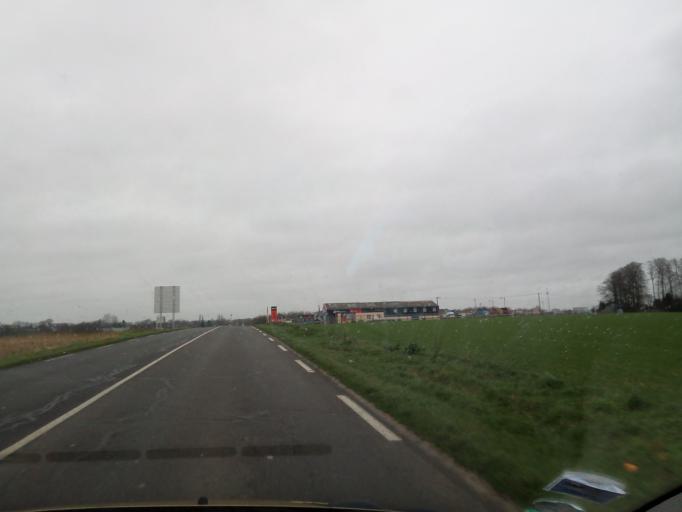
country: FR
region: Haute-Normandie
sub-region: Departement de la Seine-Maritime
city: Auzebosc
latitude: 49.6000
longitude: 0.7383
